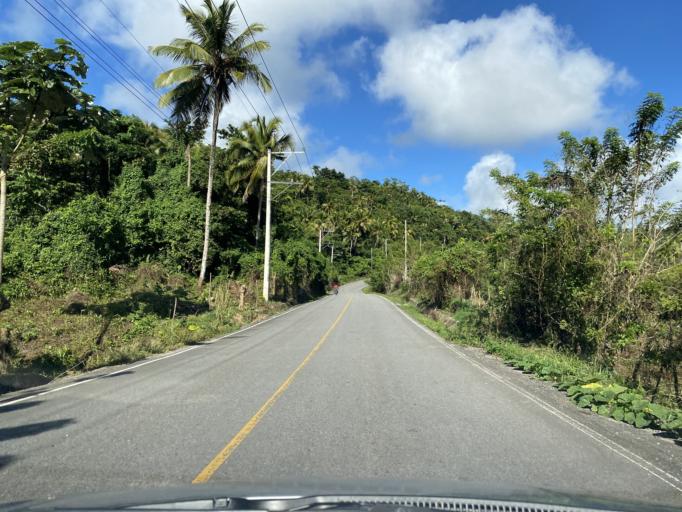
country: DO
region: Samana
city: Sanchez
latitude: 19.2548
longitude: -69.5804
